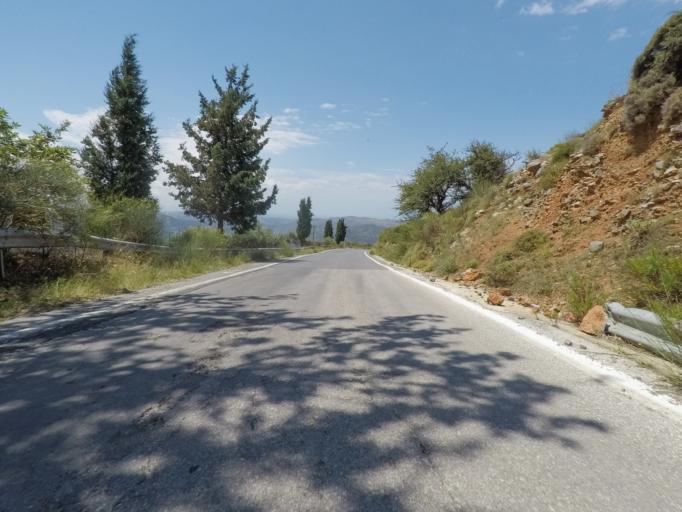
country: GR
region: Crete
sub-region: Nomos Irakleiou
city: Mokhos
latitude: 35.2145
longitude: 25.4596
